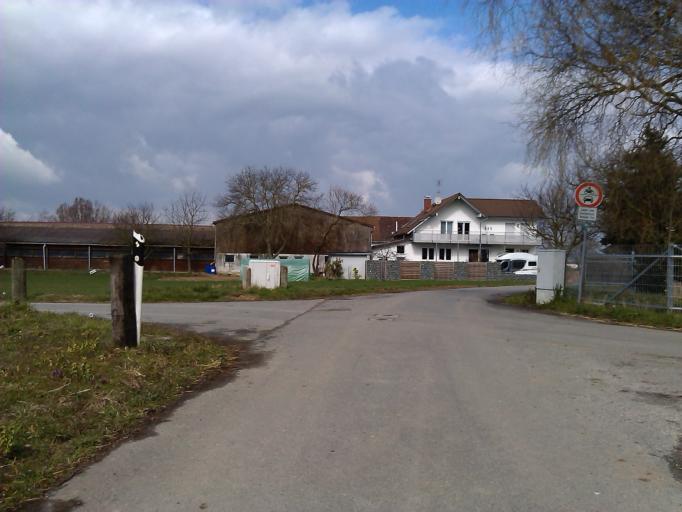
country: DE
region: Hesse
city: Pfungstadt
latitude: 49.7865
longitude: 8.5969
